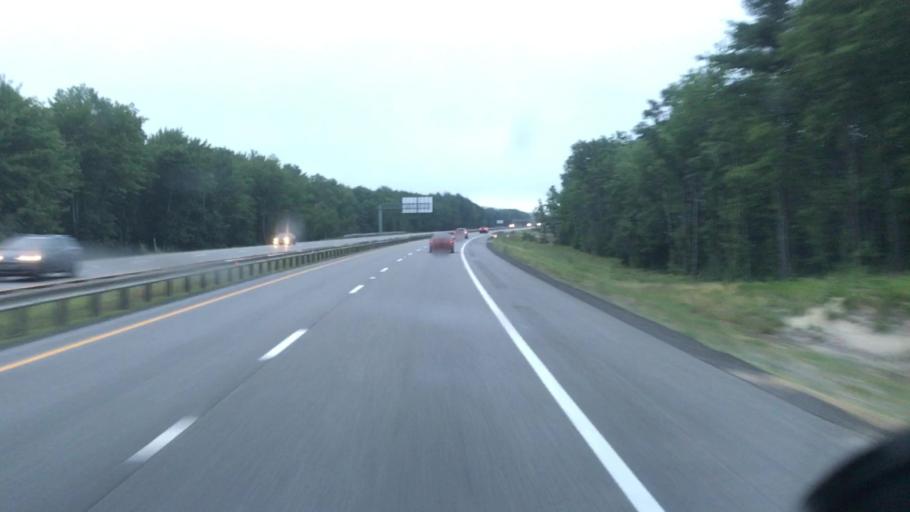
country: US
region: Maine
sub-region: Cumberland County
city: New Gloucester
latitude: 43.9502
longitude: -70.3322
